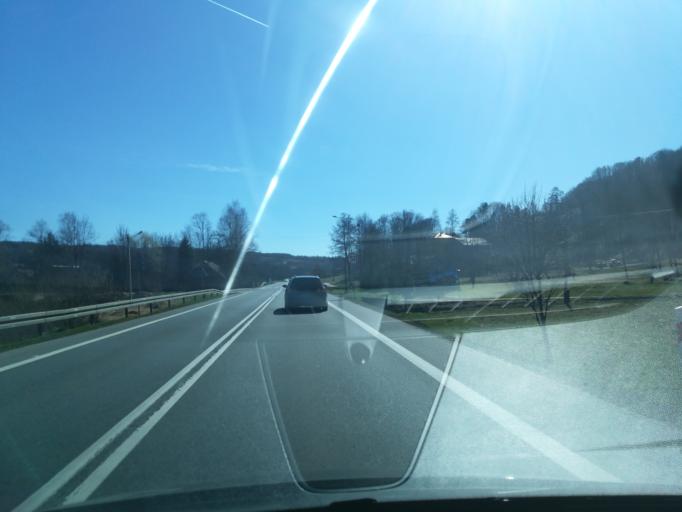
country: PL
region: Subcarpathian Voivodeship
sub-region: Powiat strzyzowski
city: Polomia
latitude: 49.8820
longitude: 21.9019
